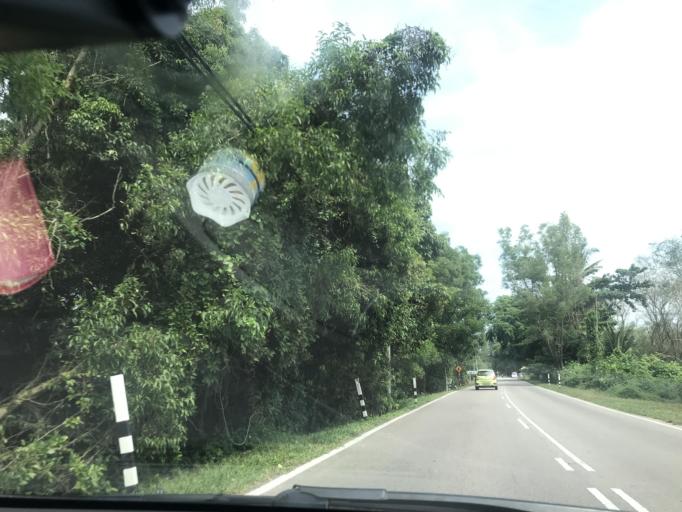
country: MY
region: Kelantan
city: Tumpat
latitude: 6.2055
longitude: 102.1480
